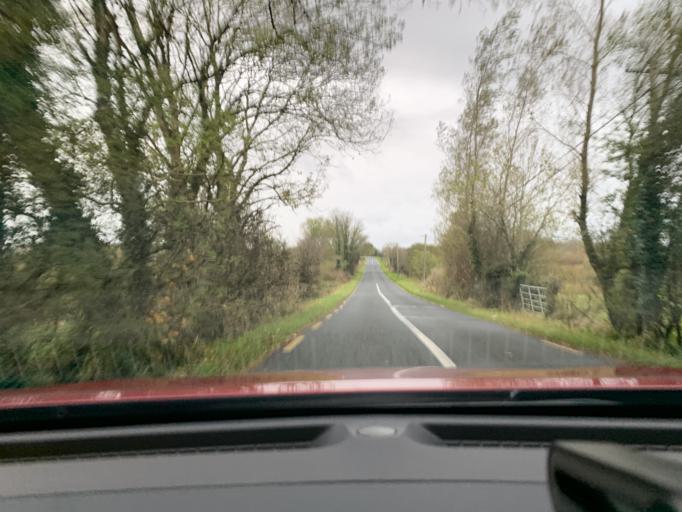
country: IE
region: Connaught
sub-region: Sligo
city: Ballymote
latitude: 54.0328
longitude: -8.5206
